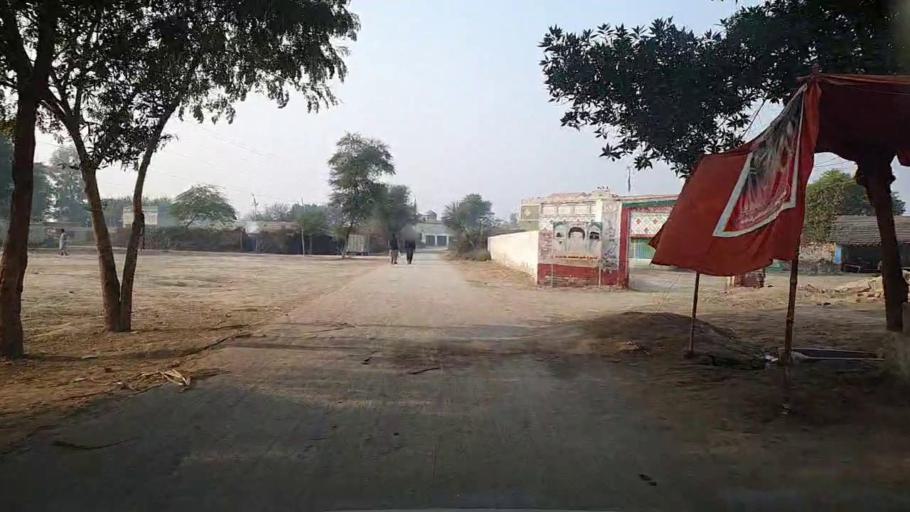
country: PK
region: Sindh
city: Kandiari
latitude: 27.0055
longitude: 68.4630
